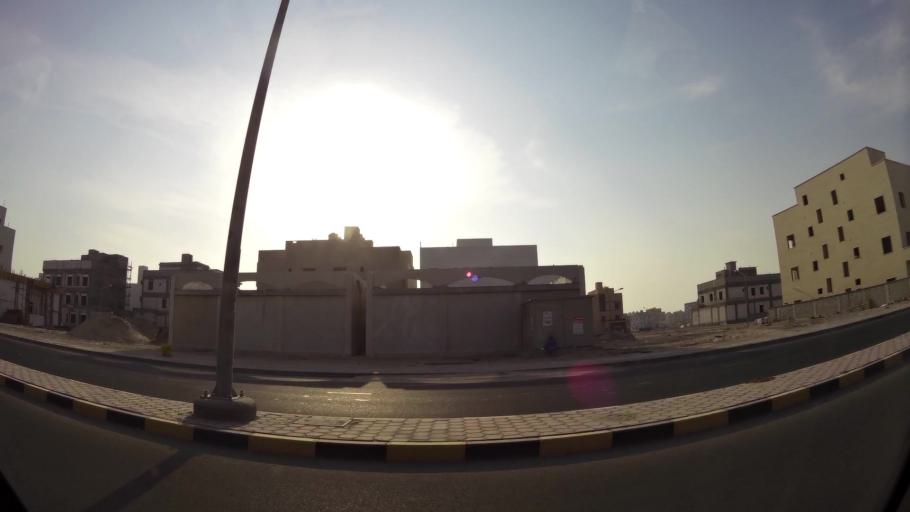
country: KW
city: Al Funaytis
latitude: 29.2240
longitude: 48.0916
